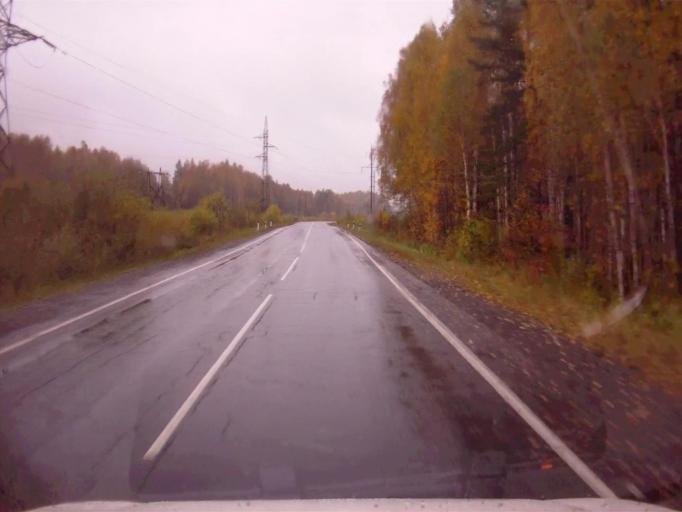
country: RU
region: Chelyabinsk
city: Verkhniy Ufaley
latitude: 55.9441
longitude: 60.4071
